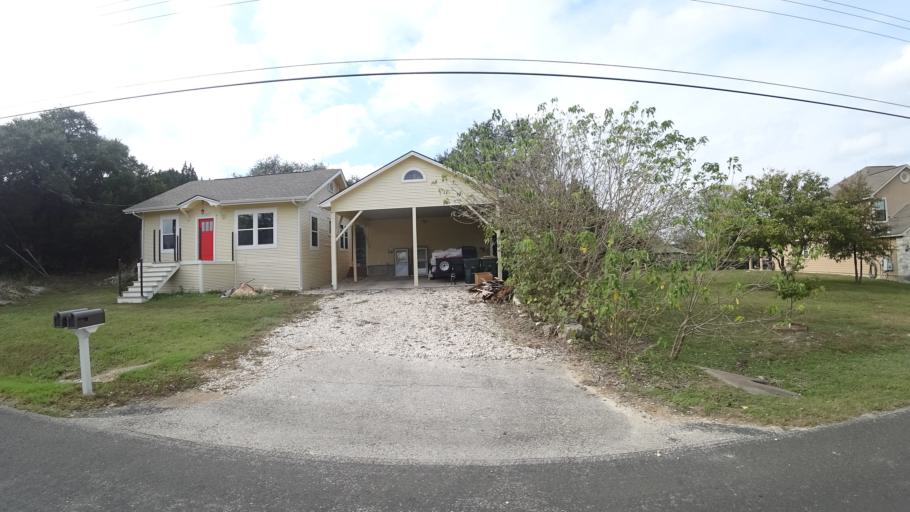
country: US
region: Texas
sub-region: Travis County
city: Hudson Bend
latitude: 30.3786
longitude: -97.9293
